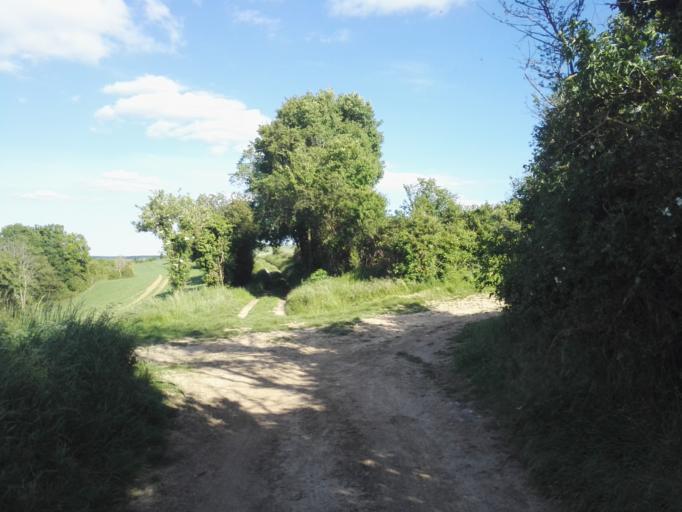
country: FR
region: Haute-Normandie
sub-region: Departement de l'Eure
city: Pacy-sur-Eure
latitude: 48.9876
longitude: 1.3782
